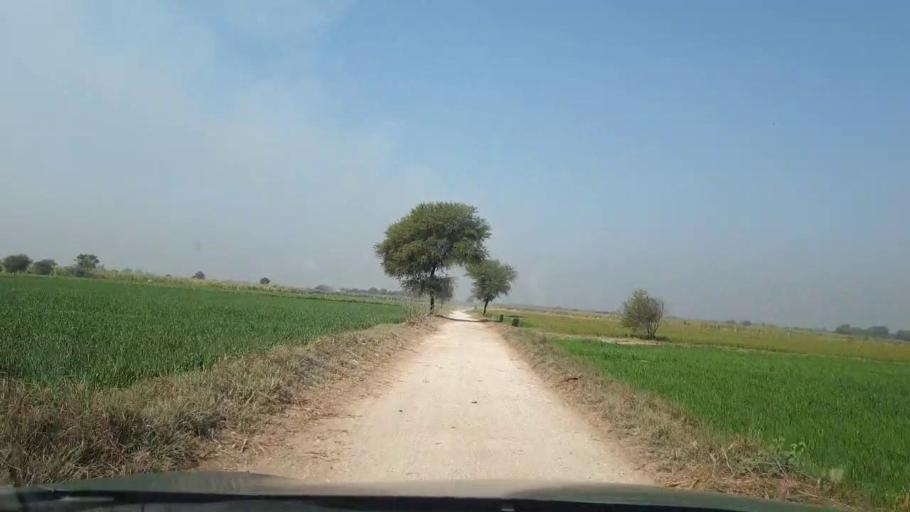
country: PK
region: Sindh
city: Tando Allahyar
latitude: 25.4733
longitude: 68.6439
